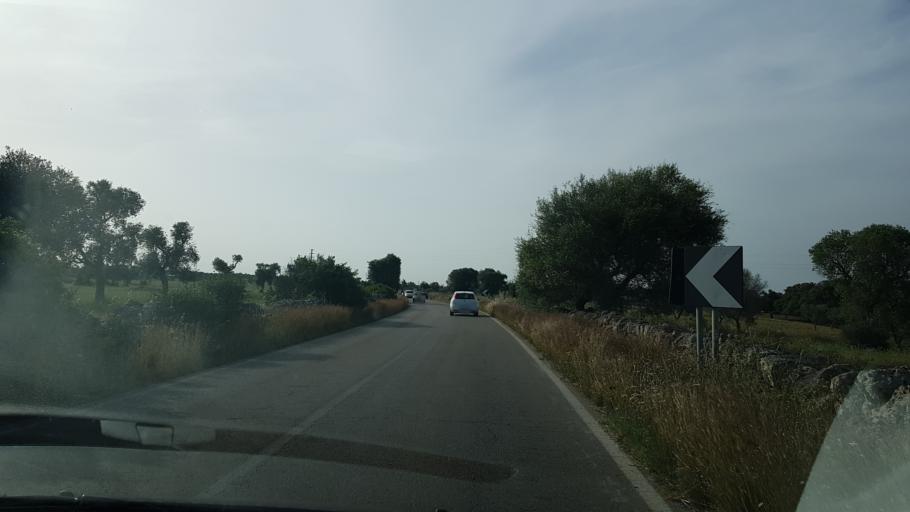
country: IT
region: Apulia
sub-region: Provincia di Lecce
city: Porto Cesareo
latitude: 40.3173
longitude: 17.8605
